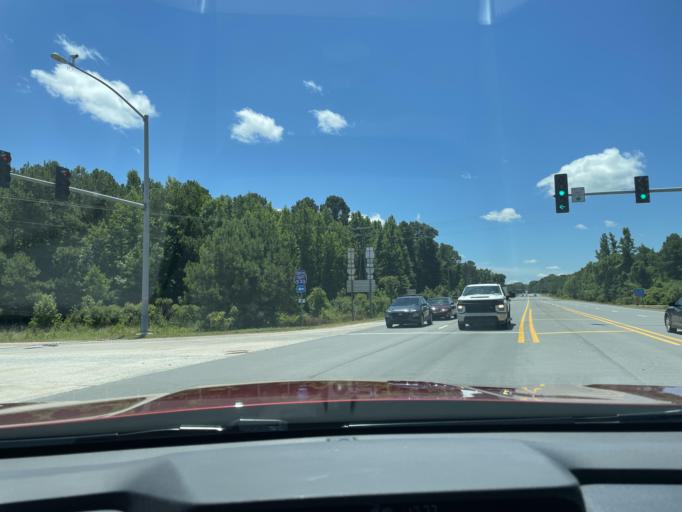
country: US
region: Arkansas
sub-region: Jefferson County
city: Pine Bluff
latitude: 34.1706
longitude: -92.0066
